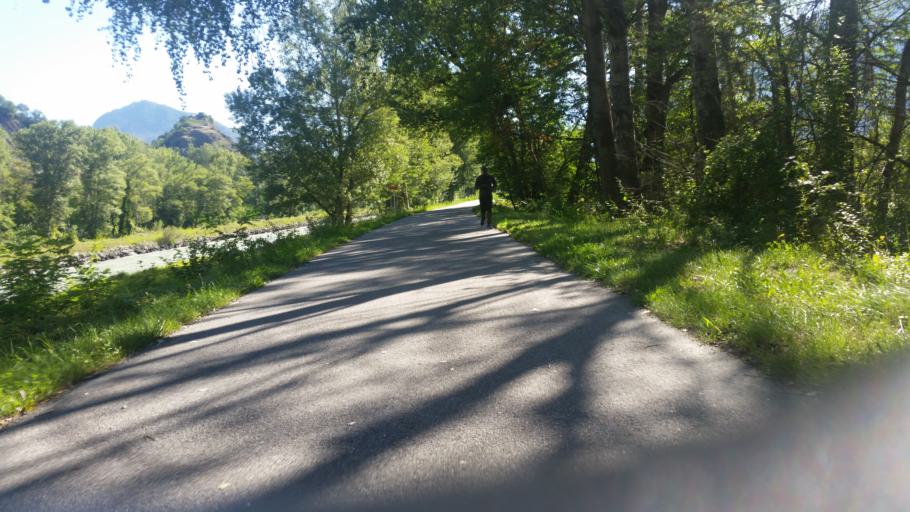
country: CH
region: Valais
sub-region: Sion District
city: Grimisuat
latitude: 46.2441
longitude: 7.3837
